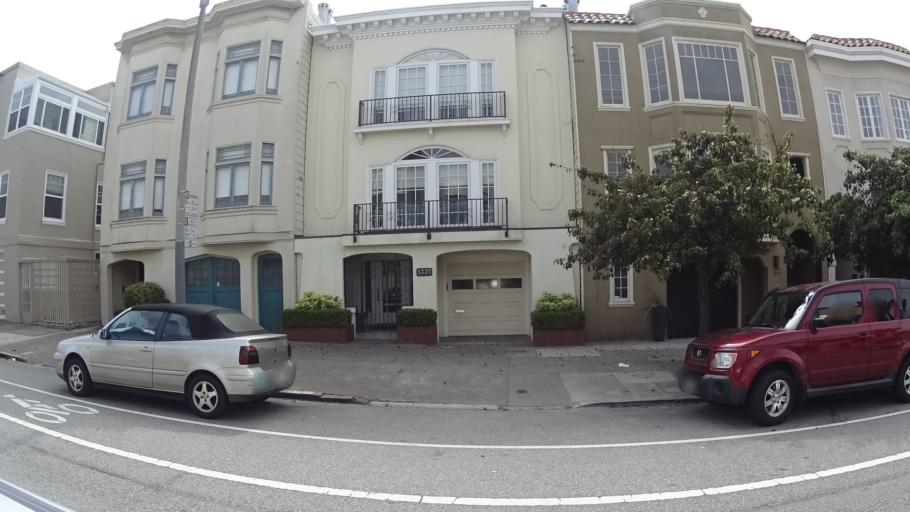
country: US
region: California
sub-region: San Francisco County
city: San Francisco
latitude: 37.8030
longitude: -122.4271
